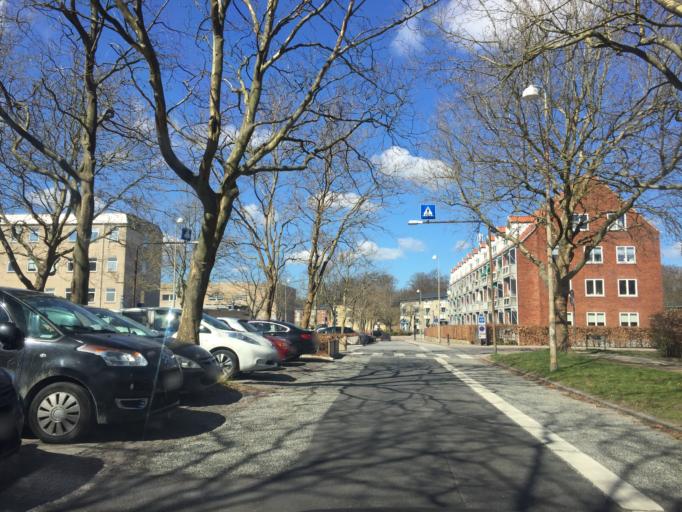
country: DK
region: Capital Region
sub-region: Rudersdal Kommune
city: Holte
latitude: 55.7945
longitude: 12.4753
